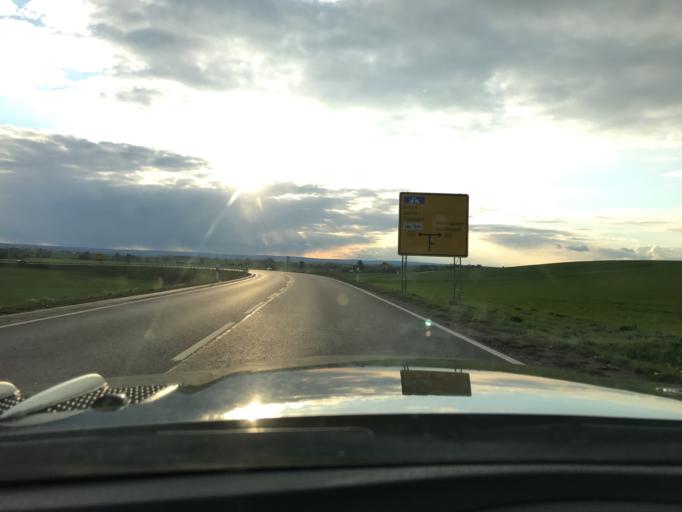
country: DE
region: Thuringia
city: Bad Langensalza
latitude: 51.1188
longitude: 10.6236
